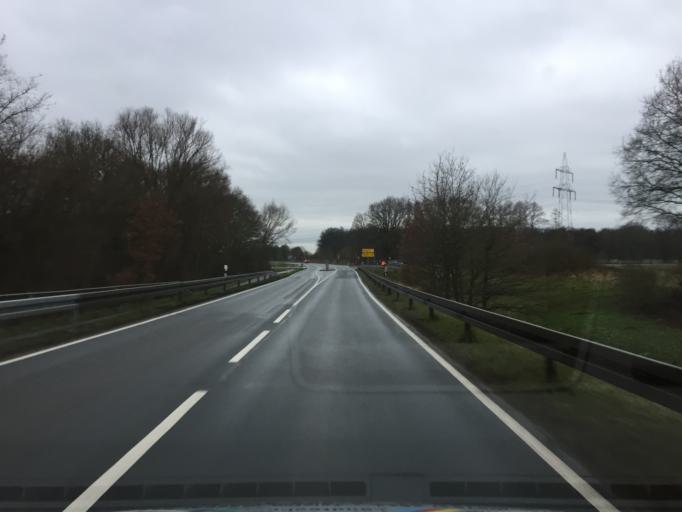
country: DE
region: Lower Saxony
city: Steyerberg
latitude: 52.5664
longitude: 9.0112
